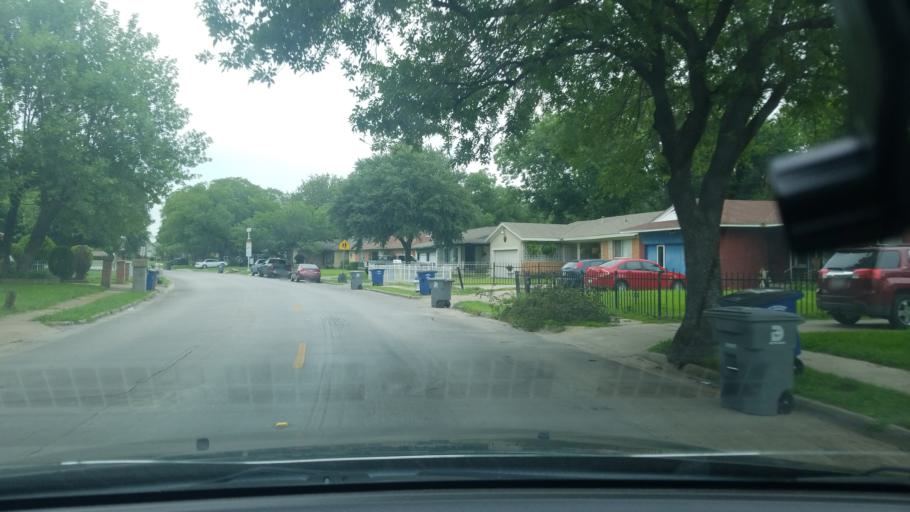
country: US
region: Texas
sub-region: Dallas County
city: Balch Springs
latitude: 32.7531
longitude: -96.6866
